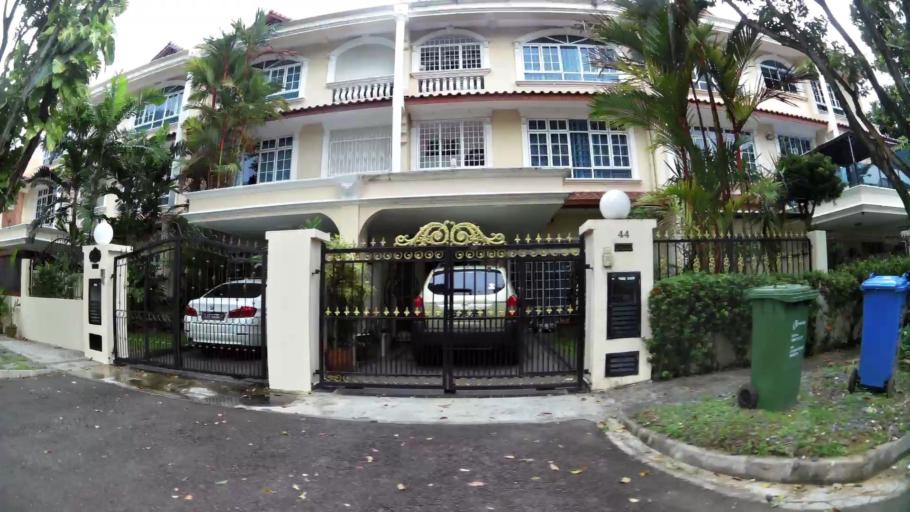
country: SG
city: Singapore
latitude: 1.3574
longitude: 103.8783
